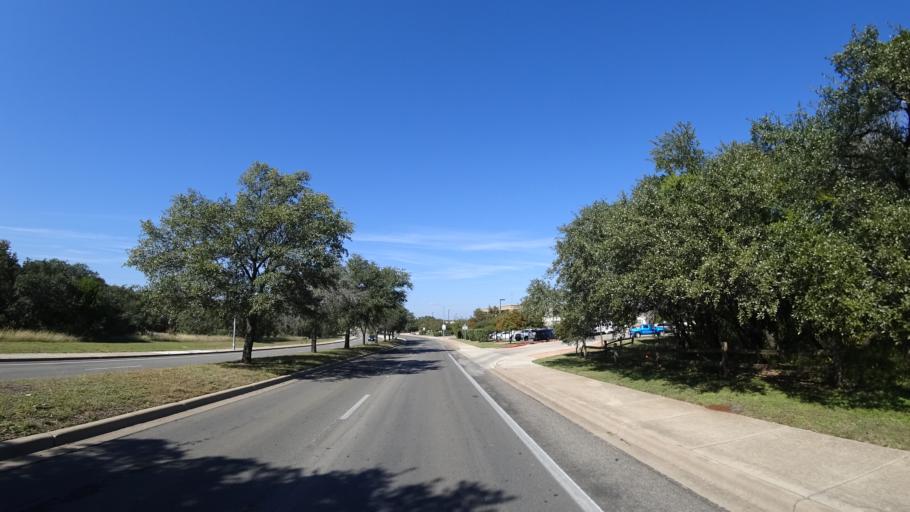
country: US
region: Texas
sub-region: Travis County
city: Shady Hollow
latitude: 30.2055
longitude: -97.8591
